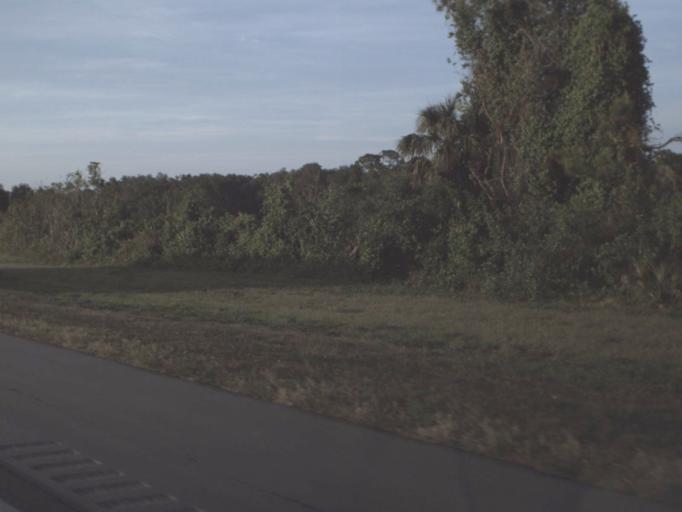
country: US
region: Florida
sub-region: Brevard County
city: Mims
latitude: 28.7102
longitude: -80.8876
